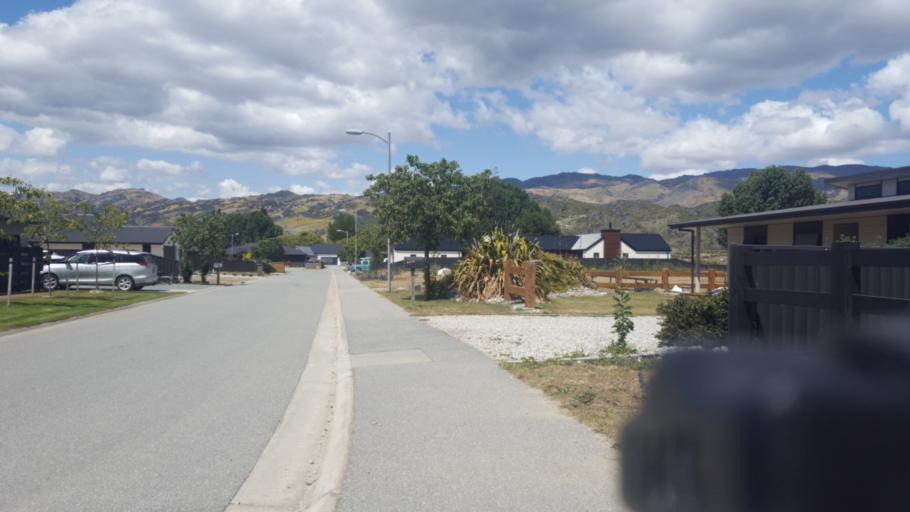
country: NZ
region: Otago
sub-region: Queenstown-Lakes District
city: Wanaka
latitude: -44.9818
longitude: 169.2350
